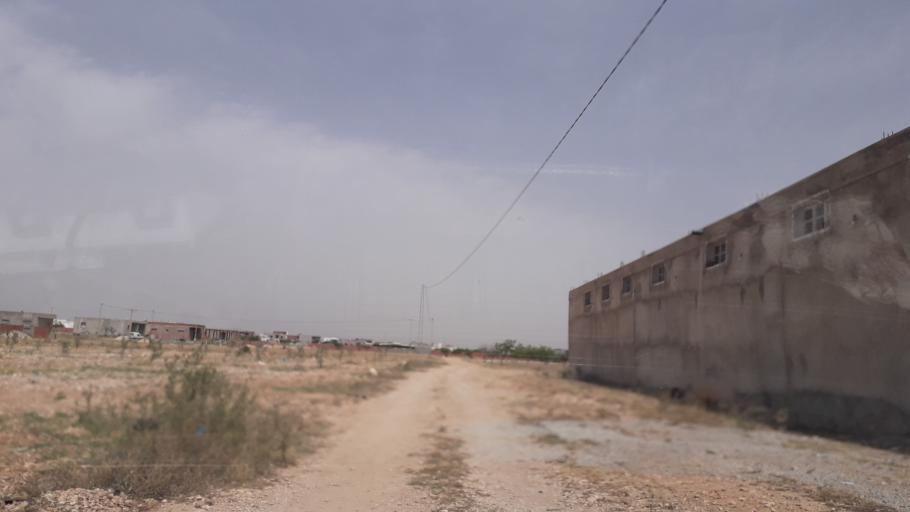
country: TN
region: Safaqis
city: Al Qarmadah
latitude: 34.8384
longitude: 10.7813
